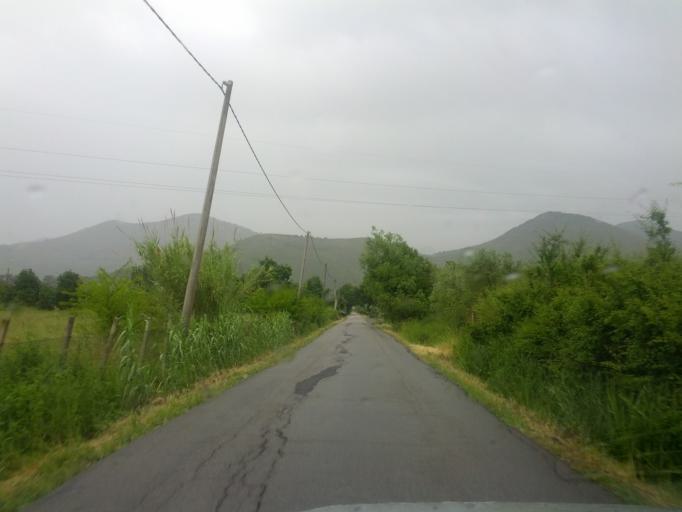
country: IT
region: Latium
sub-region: Provincia di Latina
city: Fondi
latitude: 41.3411
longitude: 13.4326
